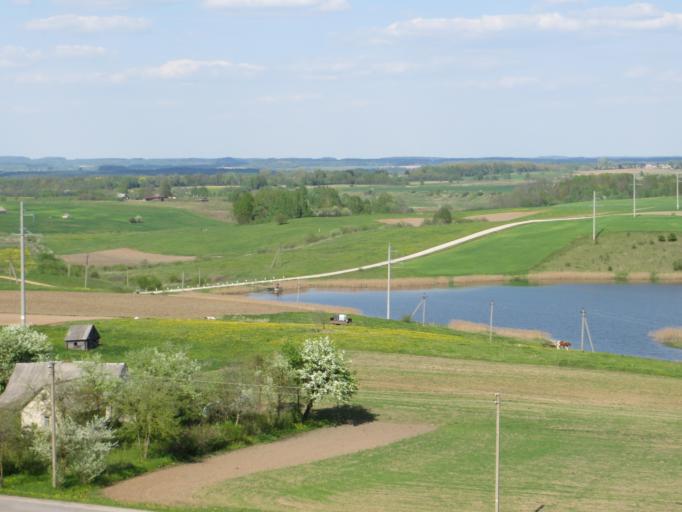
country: LT
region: Utenos apskritis
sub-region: Anyksciai
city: Anyksciai
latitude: 55.3716
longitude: 25.0340
